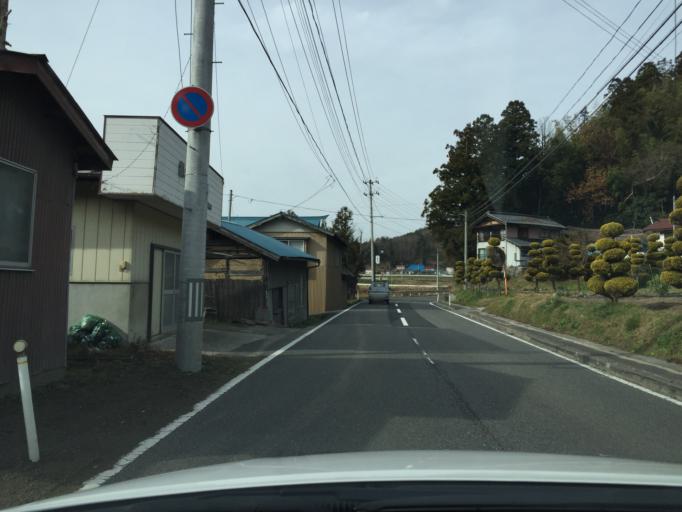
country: JP
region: Fukushima
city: Funehikimachi-funehiki
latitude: 37.3676
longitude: 140.6022
